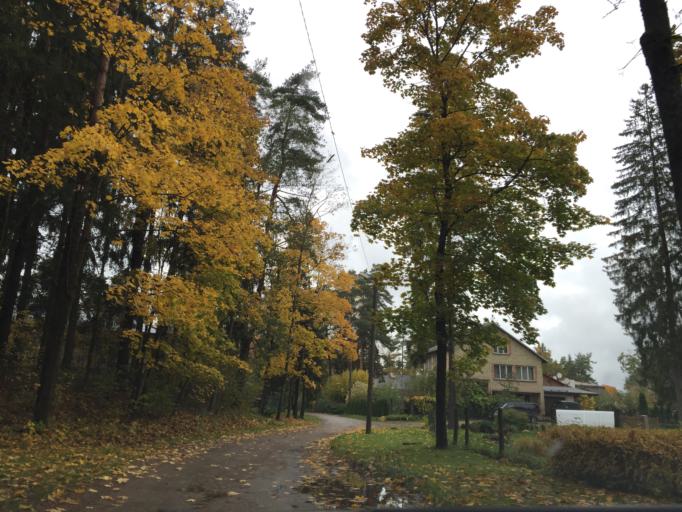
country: LV
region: Ogre
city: Ogre
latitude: 56.8092
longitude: 24.6293
